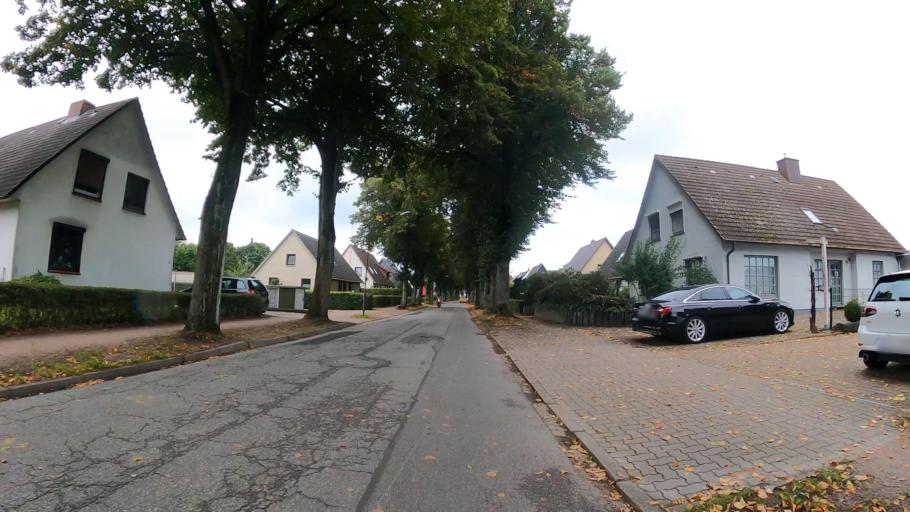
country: DE
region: Schleswig-Holstein
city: Tornesch
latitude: 53.6955
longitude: 9.7224
